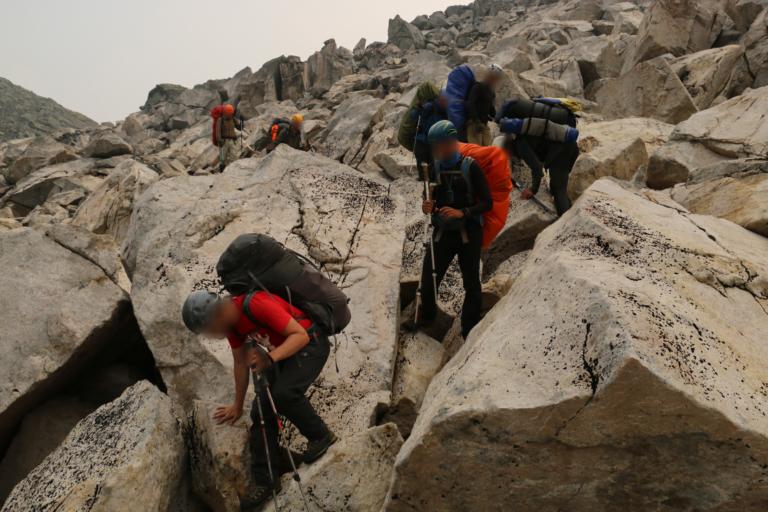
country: RU
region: Respublika Buryatiya
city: Kichera
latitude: 56.2300
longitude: 110.8655
